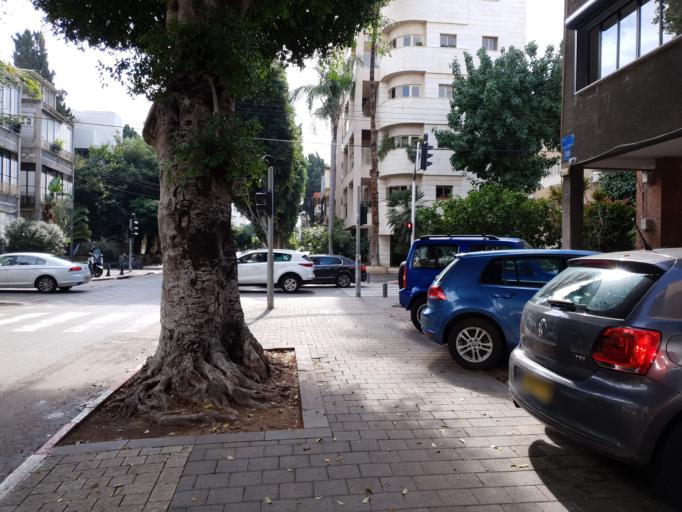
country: IL
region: Tel Aviv
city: Tel Aviv
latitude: 32.0817
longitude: 34.7757
